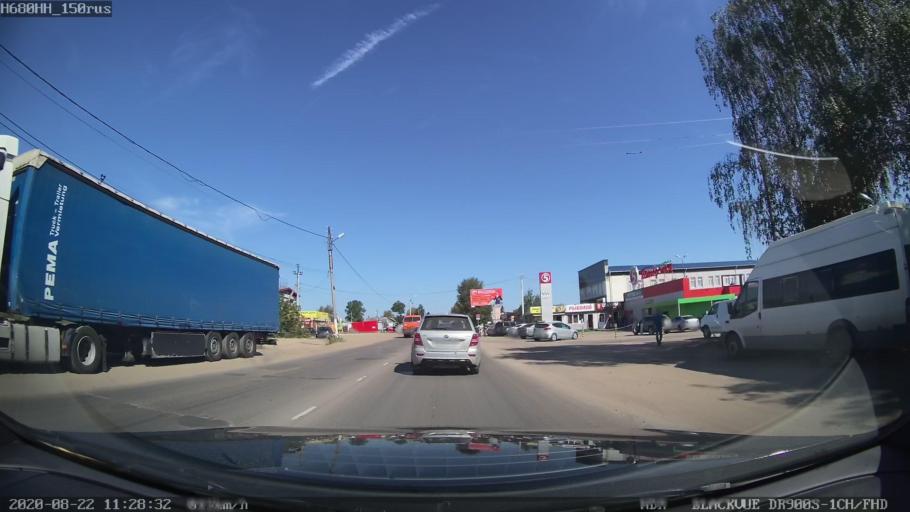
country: RU
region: Tverskaya
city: Tver
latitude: 56.8847
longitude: 35.9277
